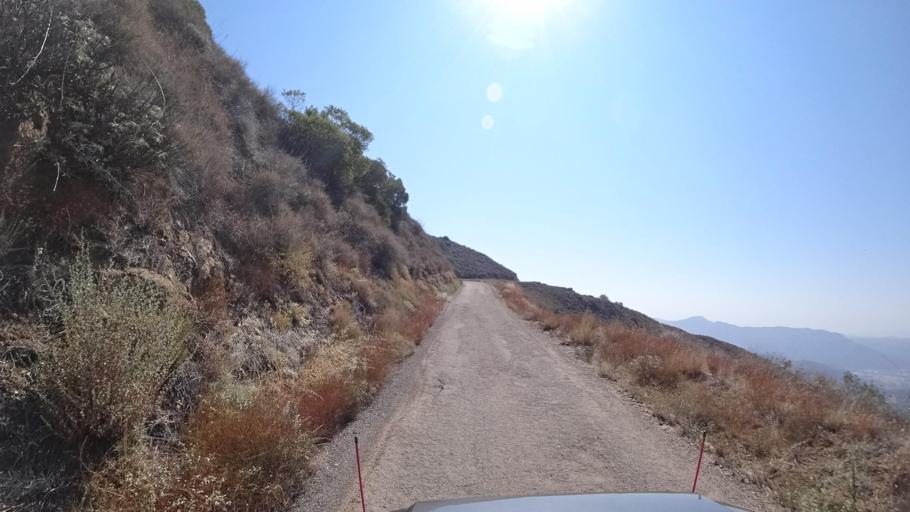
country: US
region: California
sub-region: Riverside County
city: Aguanga
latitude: 33.3338
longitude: -116.9486
